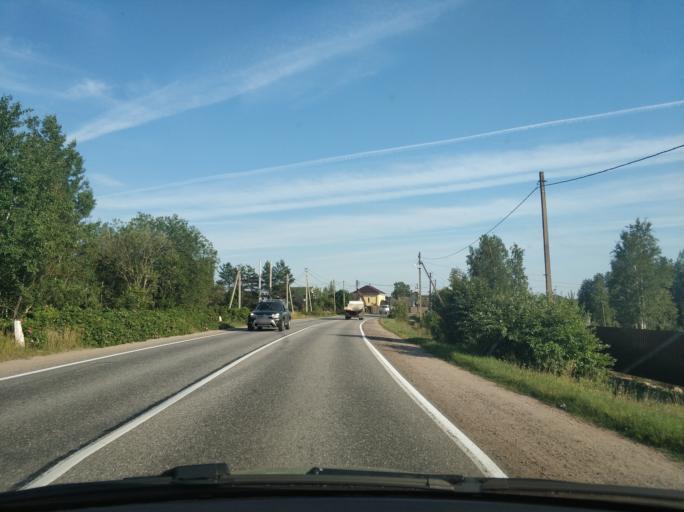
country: RU
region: Leningrad
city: Borisova Griva
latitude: 60.0907
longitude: 31.0178
